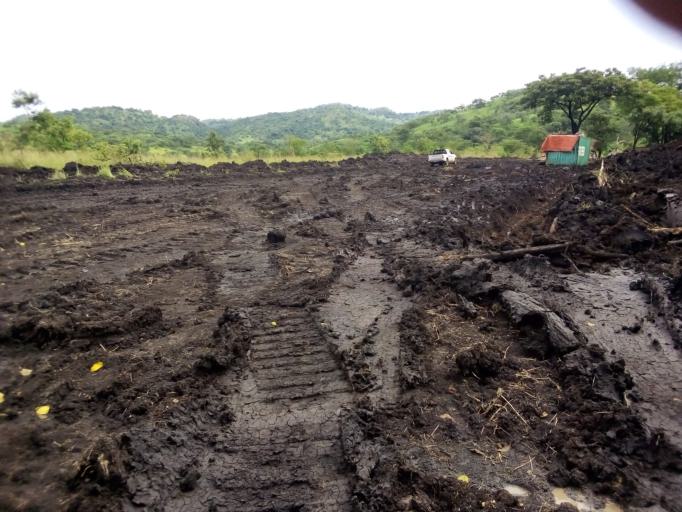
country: ET
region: Oromiya
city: Jima
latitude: 7.2163
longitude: 37.1331
